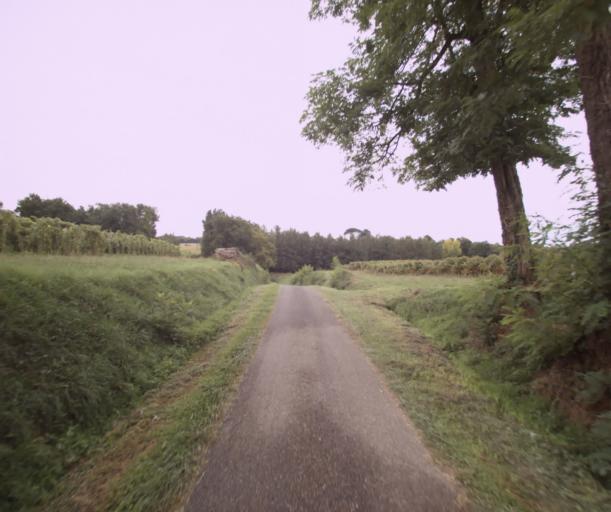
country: FR
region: Midi-Pyrenees
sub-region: Departement du Gers
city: Cazaubon
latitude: 43.8701
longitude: -0.0542
